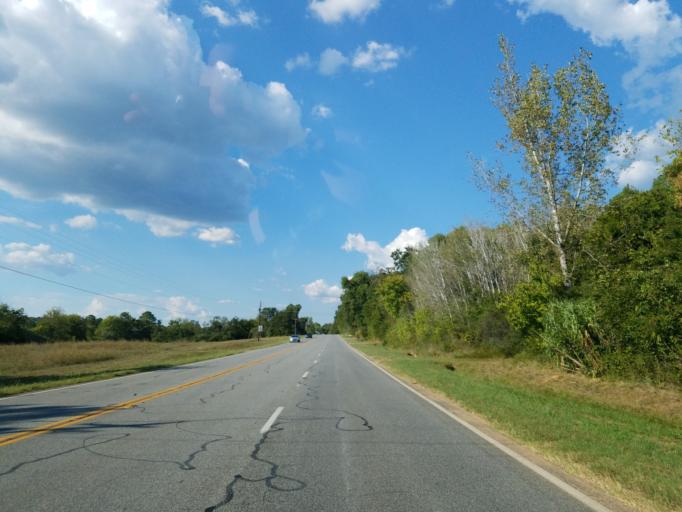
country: US
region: Georgia
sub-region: Bartow County
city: Rydal
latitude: 34.4798
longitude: -84.7065
